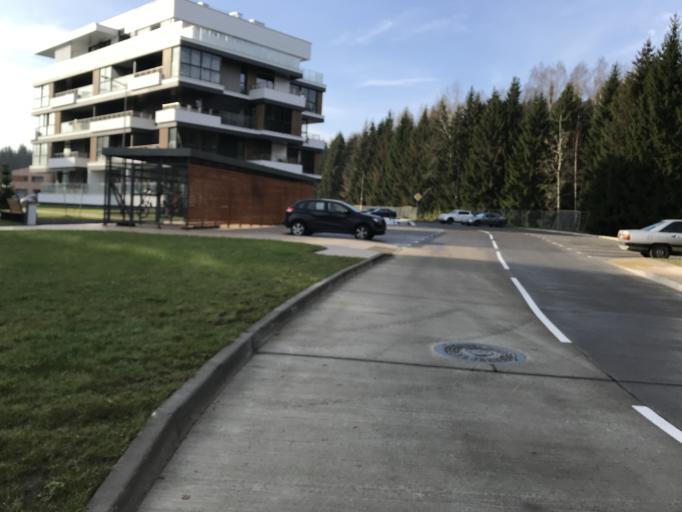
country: BY
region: Minsk
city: Khatsyezhyna
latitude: 53.9482
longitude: 27.3308
